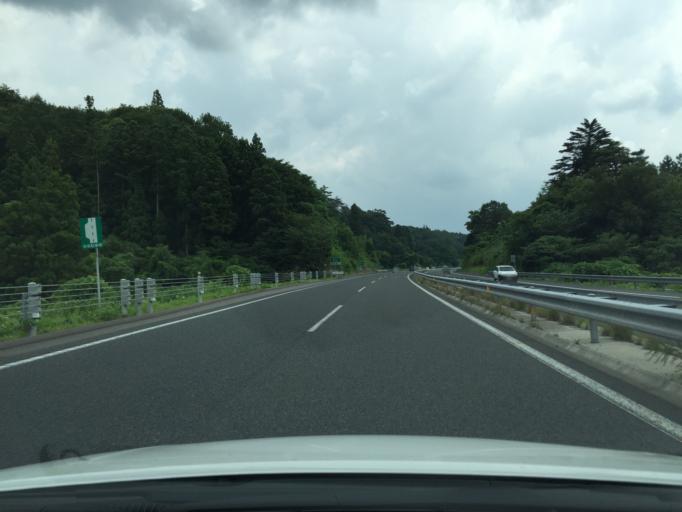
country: JP
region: Fukushima
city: Funehikimachi-funehiki
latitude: 37.3347
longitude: 140.6142
